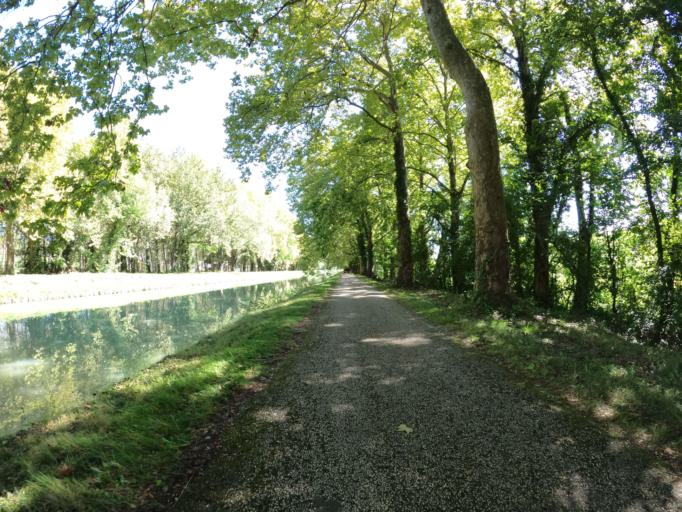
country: FR
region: Midi-Pyrenees
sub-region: Departement du Tarn-et-Garonne
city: Valence
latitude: 44.1109
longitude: 0.8740
